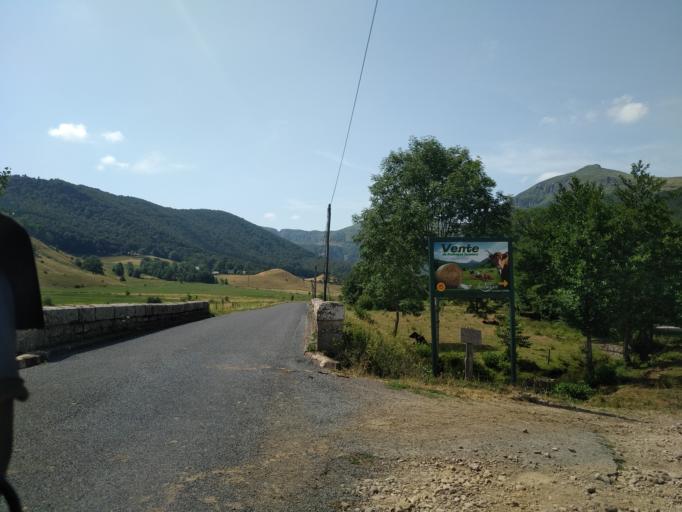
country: FR
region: Auvergne
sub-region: Departement du Cantal
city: Riom-es-Montagnes
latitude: 45.1441
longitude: 2.6985
